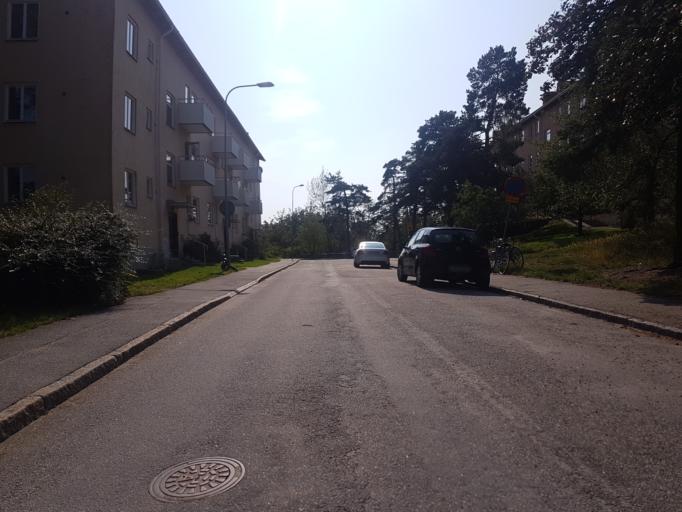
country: SE
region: Stockholm
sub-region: Nacka Kommun
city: Nacka
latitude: 59.2967
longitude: 18.1144
